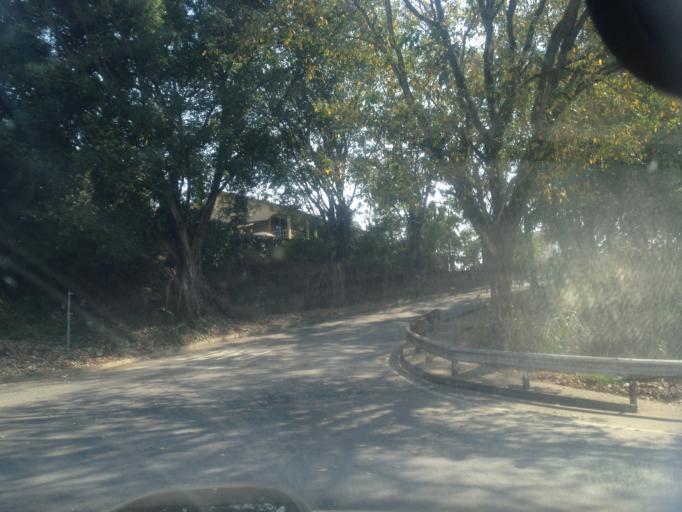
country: BR
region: Rio de Janeiro
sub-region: Porto Real
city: Porto Real
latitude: -22.4518
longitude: -44.3066
